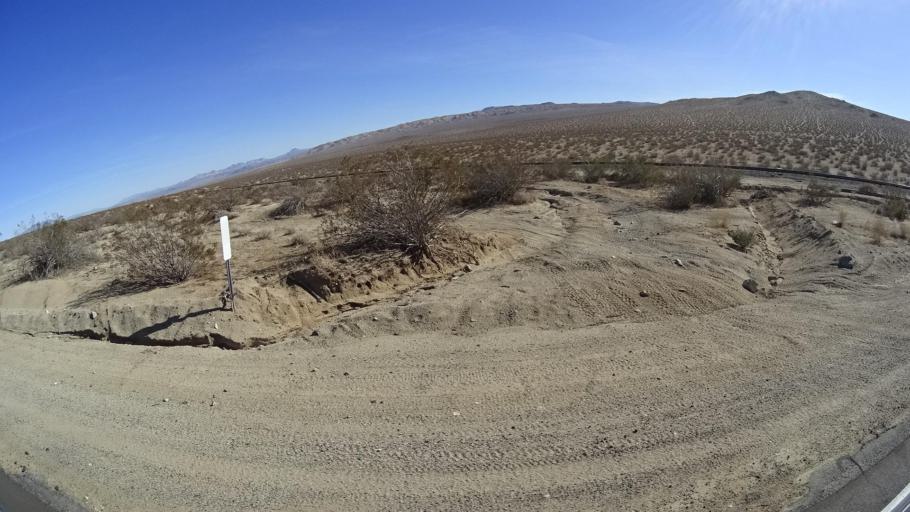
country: US
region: California
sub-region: Kern County
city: Ridgecrest
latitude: 35.5095
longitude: -117.6138
